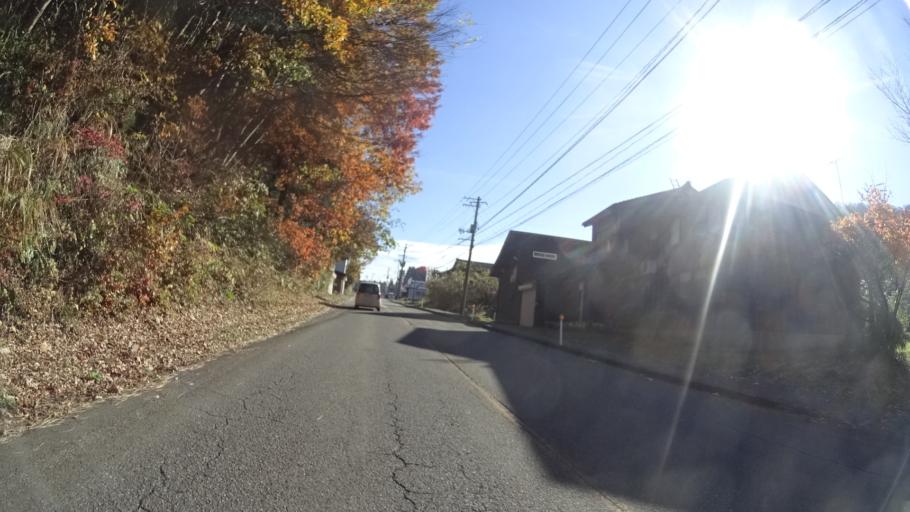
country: JP
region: Niigata
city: Tochio-honcho
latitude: 37.4833
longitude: 138.9826
